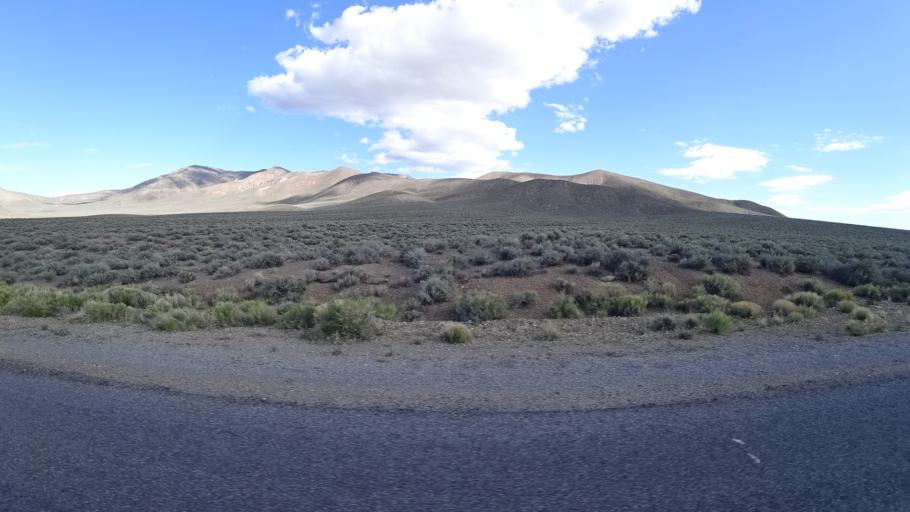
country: US
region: California
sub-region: San Bernardino County
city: Searles Valley
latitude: 36.3349
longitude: -117.1410
